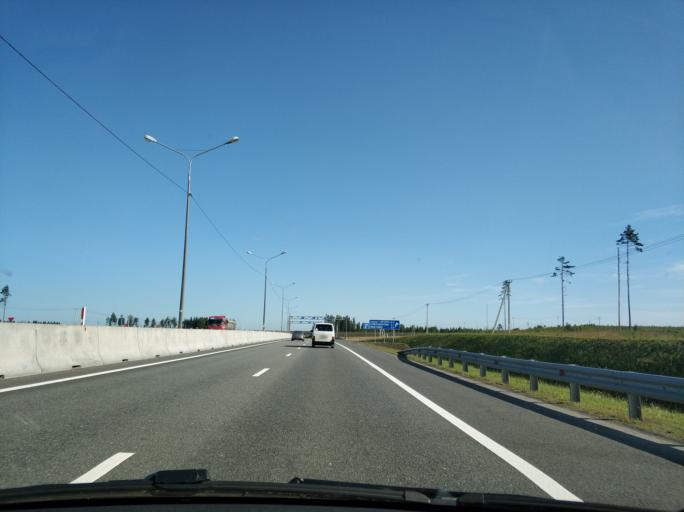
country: RU
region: Leningrad
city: Sosnovo
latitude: 60.4981
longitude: 30.1959
